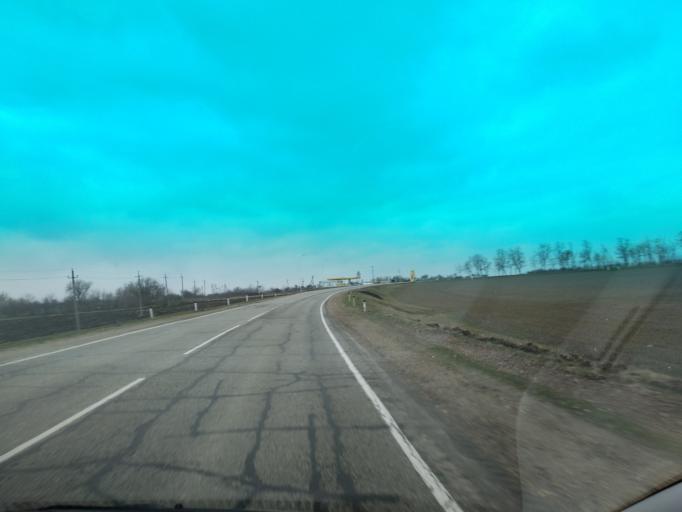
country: RU
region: Krasnodarskiy
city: Novomalorossiyskaya
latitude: 45.7099
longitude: 39.8635
